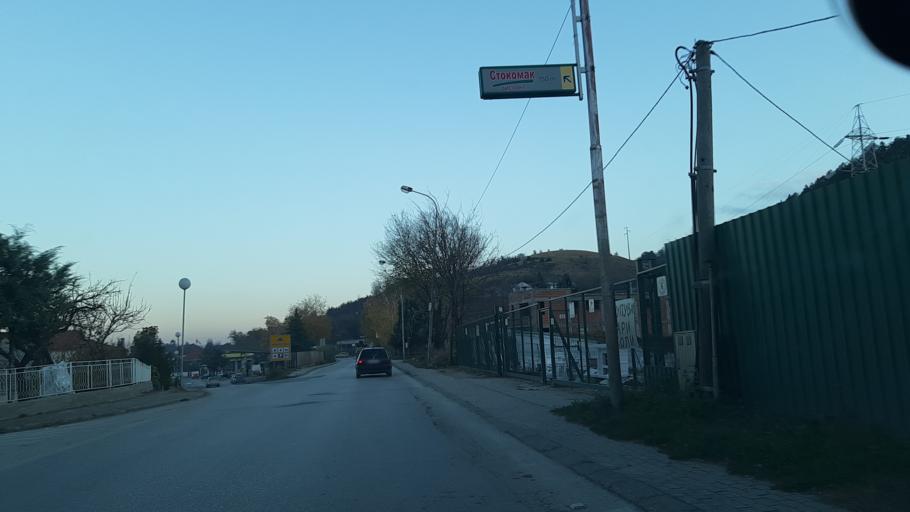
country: MK
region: Kisela Voda
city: Kisela Voda
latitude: 41.9370
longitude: 21.5113
